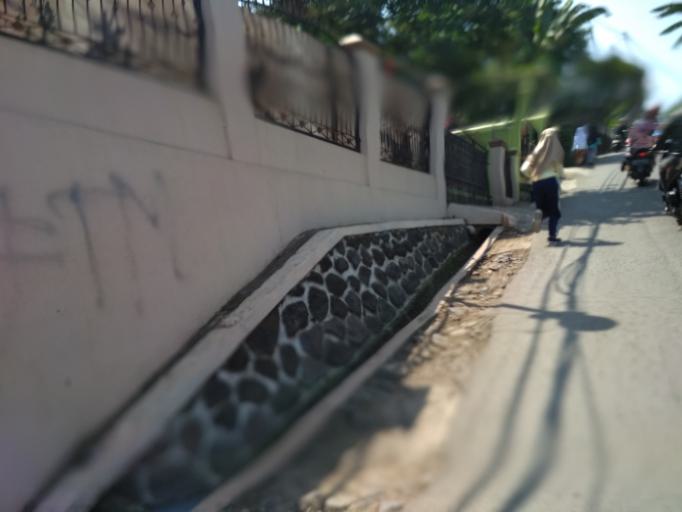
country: ID
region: West Java
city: Ciampea
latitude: -6.5590
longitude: 106.7407
